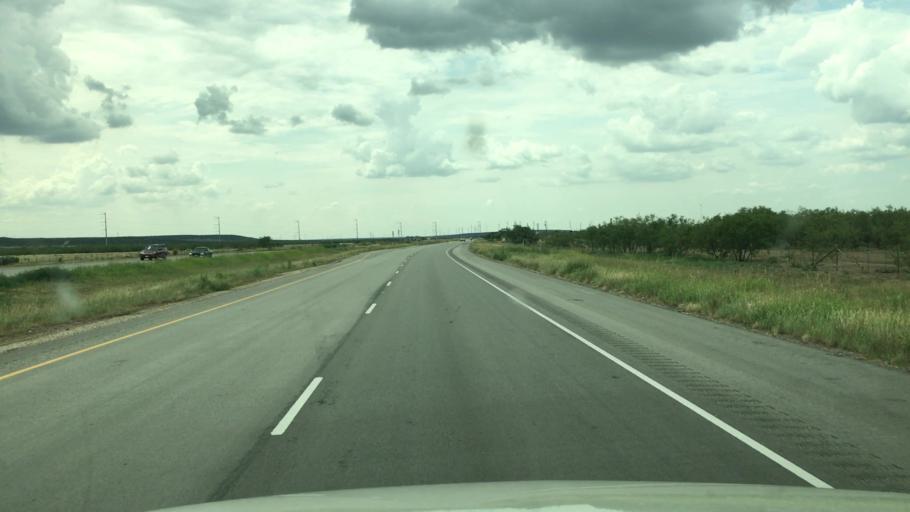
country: US
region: Texas
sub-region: Sterling County
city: Sterling City
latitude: 31.9631
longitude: -101.2205
